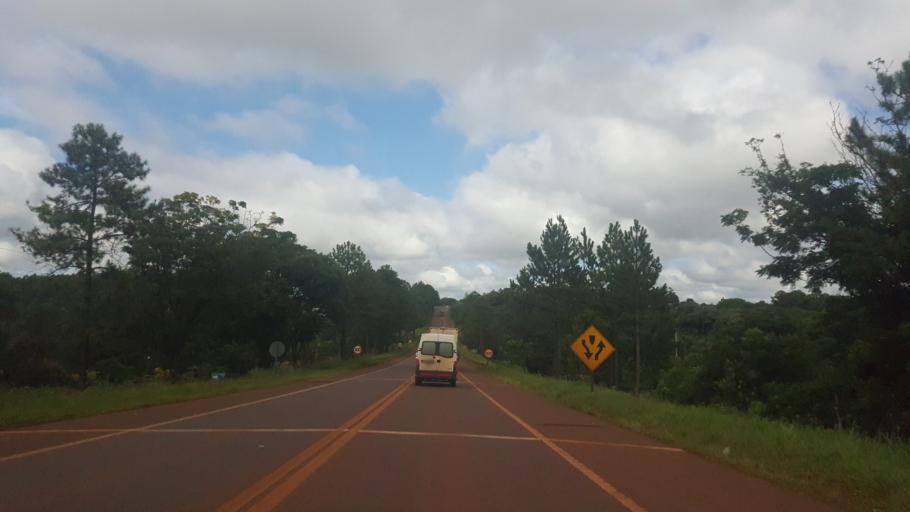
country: AR
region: Misiones
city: Aristobulo del Valle
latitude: -27.0842
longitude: -54.8221
